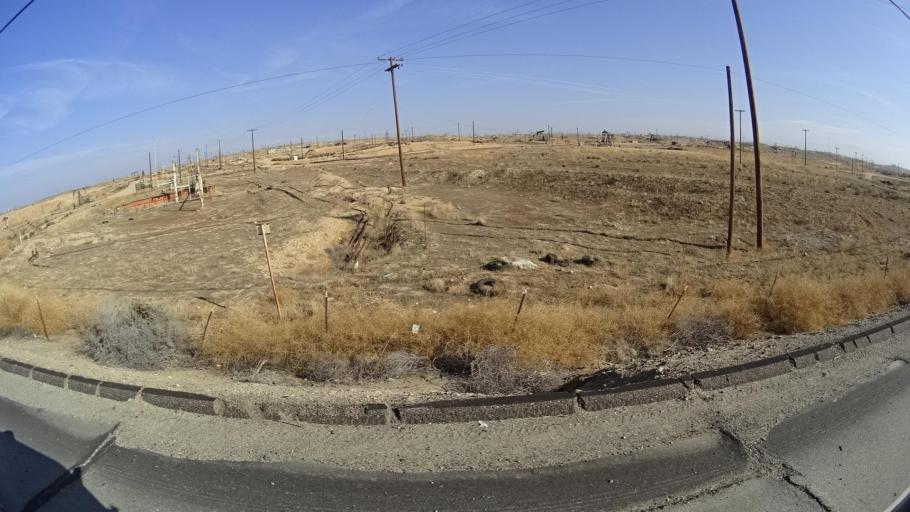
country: US
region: California
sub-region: Kern County
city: Oildale
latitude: 35.4639
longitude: -119.0558
